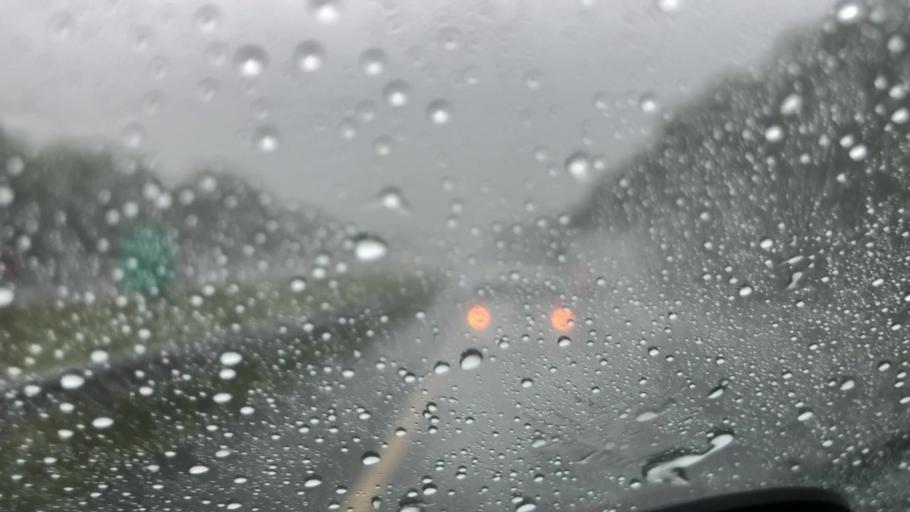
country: US
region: Massachusetts
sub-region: Hampden County
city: Westfield
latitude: 42.1569
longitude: -72.8024
